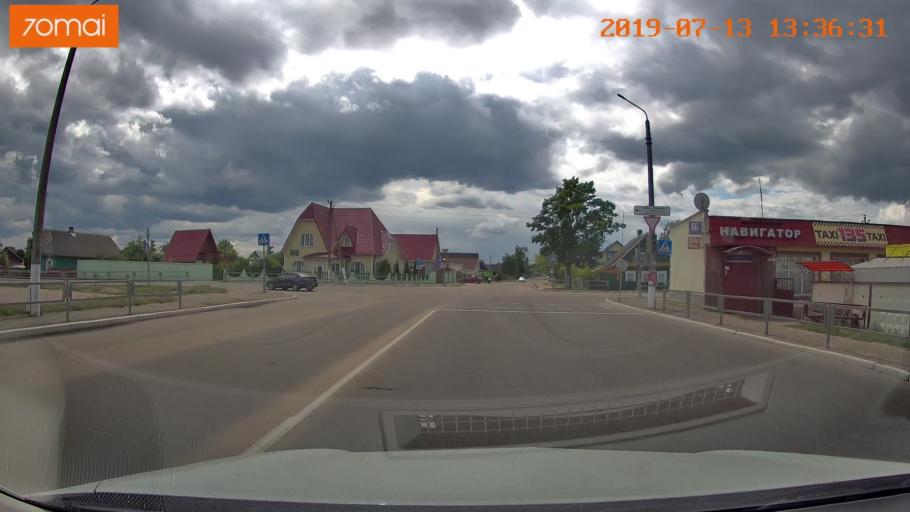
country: BY
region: Mogilev
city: Asipovichy
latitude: 53.3015
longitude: 28.6234
